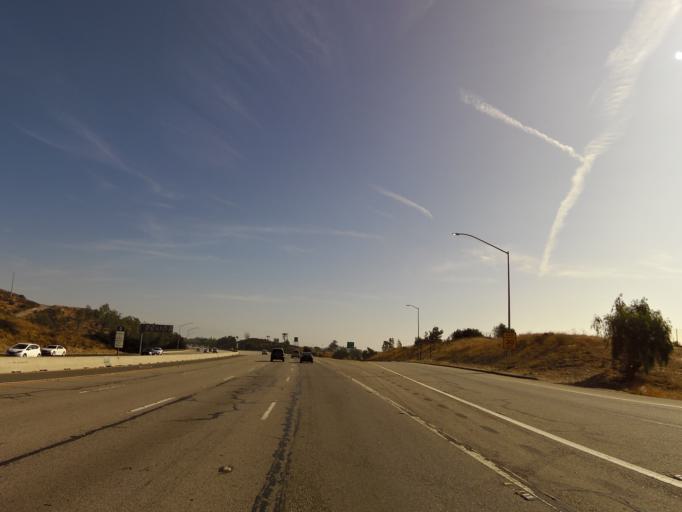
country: US
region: California
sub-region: Los Angeles County
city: Chatsworth
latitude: 34.2740
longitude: -118.5943
